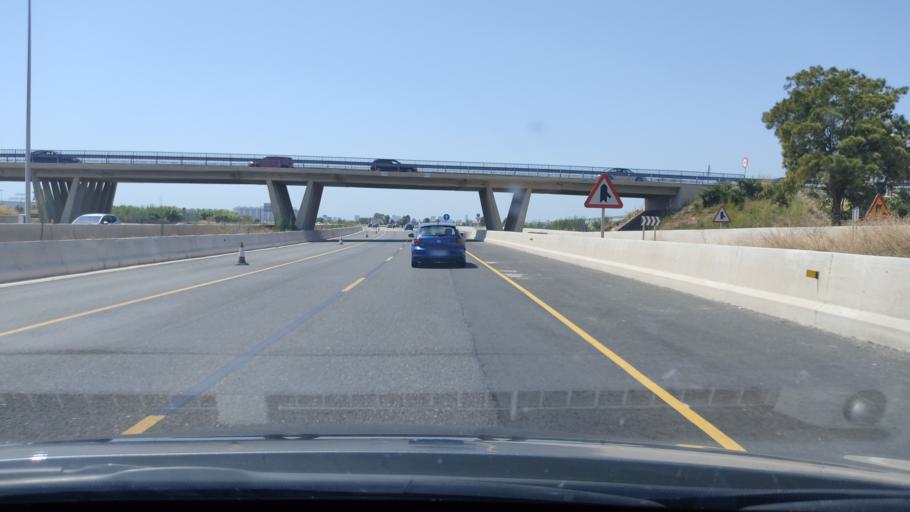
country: ES
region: Valencia
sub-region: Provincia de Valencia
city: Meliana
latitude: 39.5093
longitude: -0.3249
